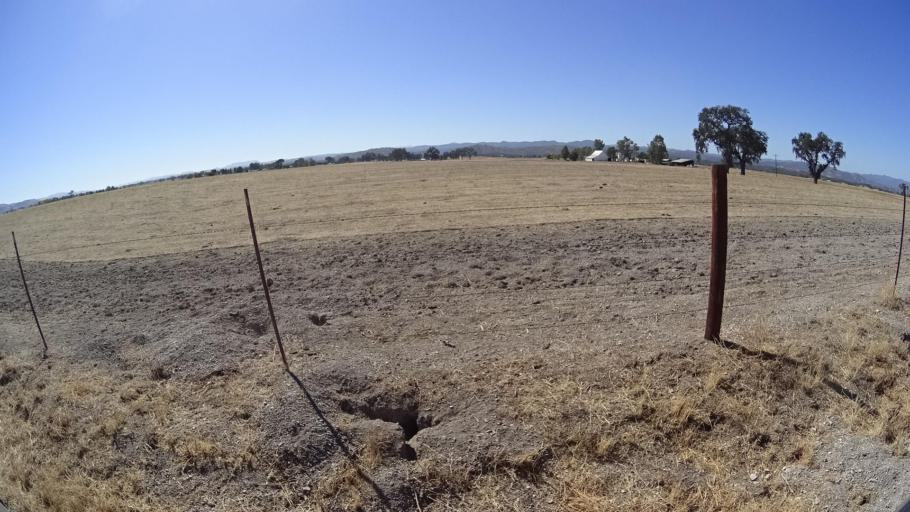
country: US
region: California
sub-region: Monterey County
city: King City
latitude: 35.9515
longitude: -121.0877
